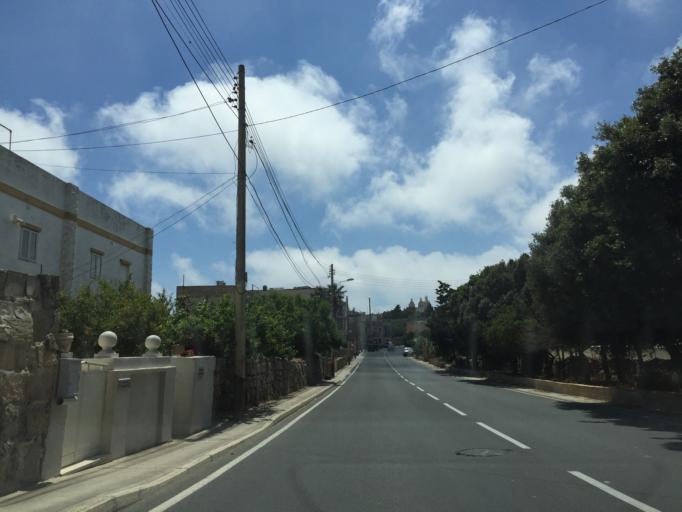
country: MT
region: Dingli
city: Dingli
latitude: 35.8634
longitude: 14.3883
